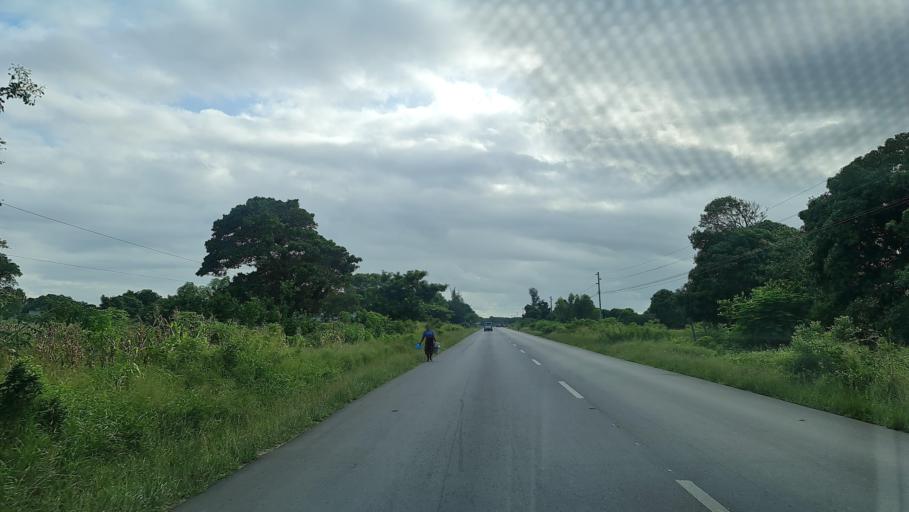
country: MZ
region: Maputo
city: Manhica
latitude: -25.4145
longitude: 32.7382
